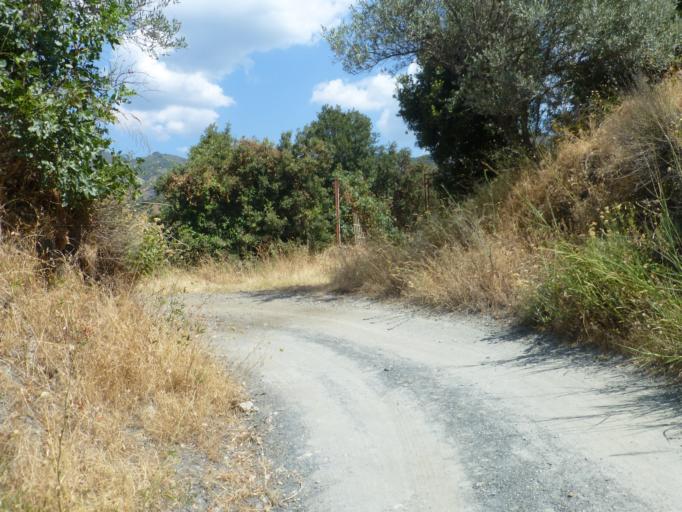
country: IT
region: Calabria
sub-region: Provincia di Reggio Calabria
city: Pazzano
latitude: 38.4794
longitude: 16.4459
